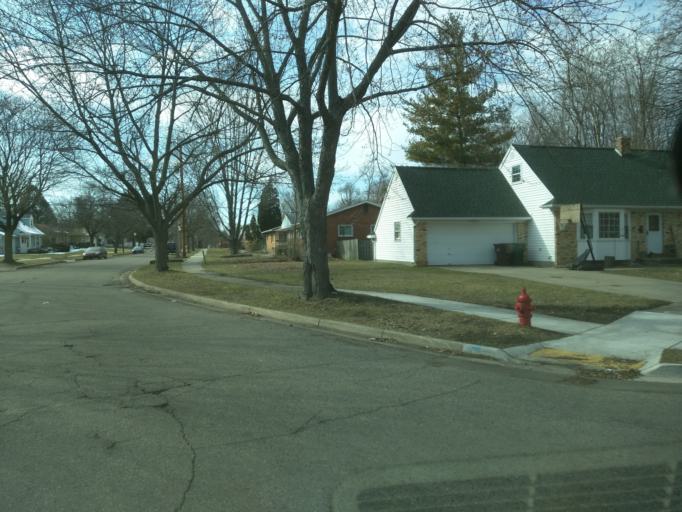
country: US
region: Michigan
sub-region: Ingham County
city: Edgemont Park
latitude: 42.7067
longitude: -84.5925
